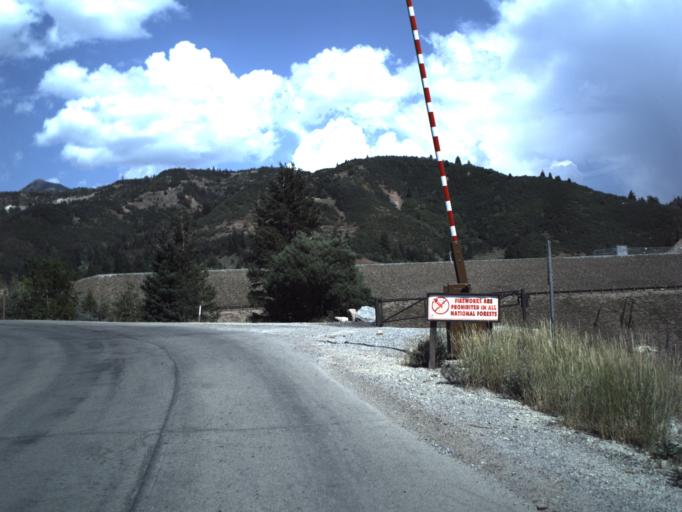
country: US
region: Utah
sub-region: Utah County
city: Highland
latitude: 40.4795
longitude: -111.6468
